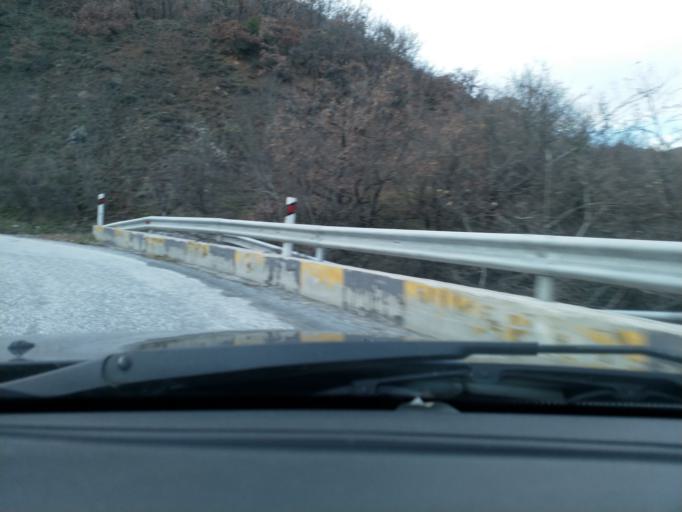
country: GR
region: Epirus
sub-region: Nomos Ioanninon
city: Metsovo
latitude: 39.8058
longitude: 21.3564
